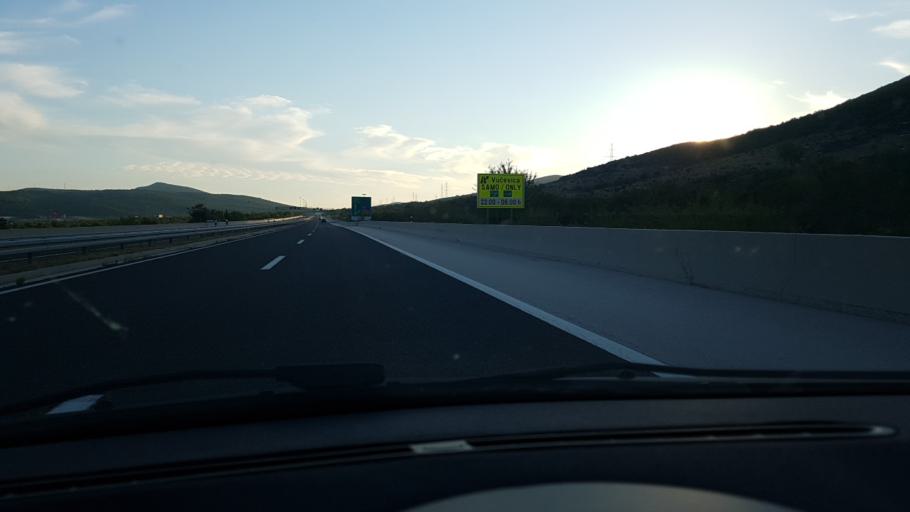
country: HR
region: Splitsko-Dalmatinska
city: Dugopolje
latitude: 43.6014
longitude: 16.5816
